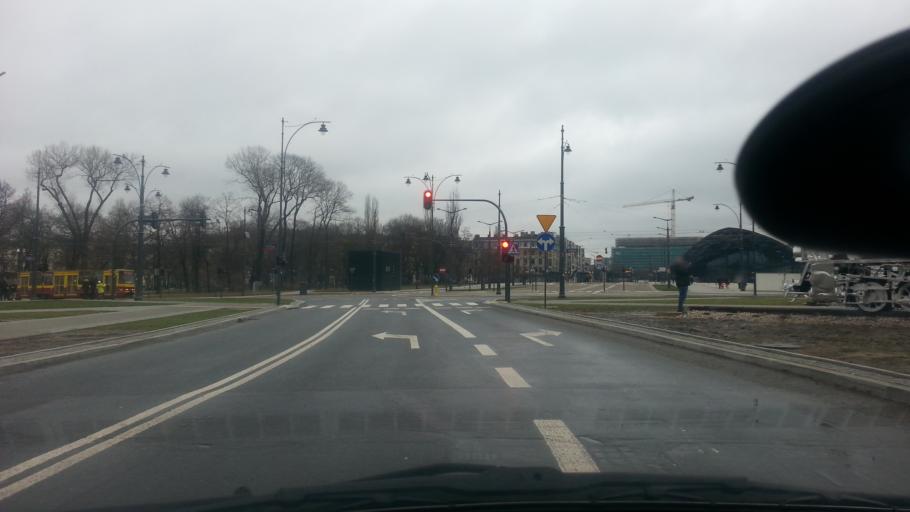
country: PL
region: Lodz Voivodeship
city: Lodz
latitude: 51.7691
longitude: 19.4635
